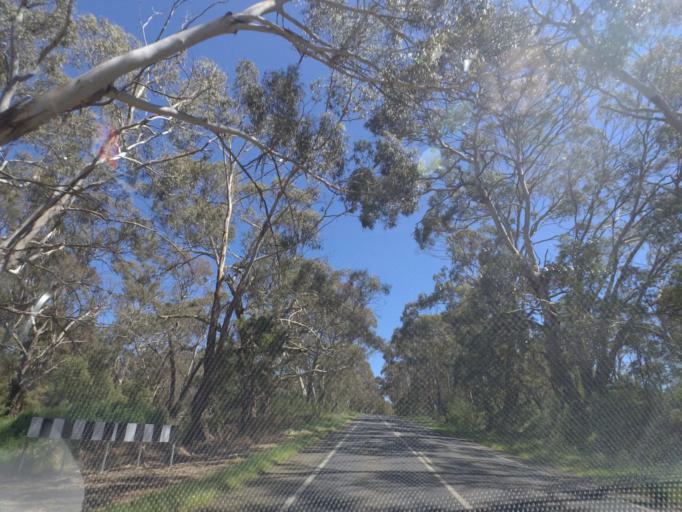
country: AU
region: Victoria
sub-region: Hume
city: Sunbury
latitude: -37.2952
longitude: 144.7998
